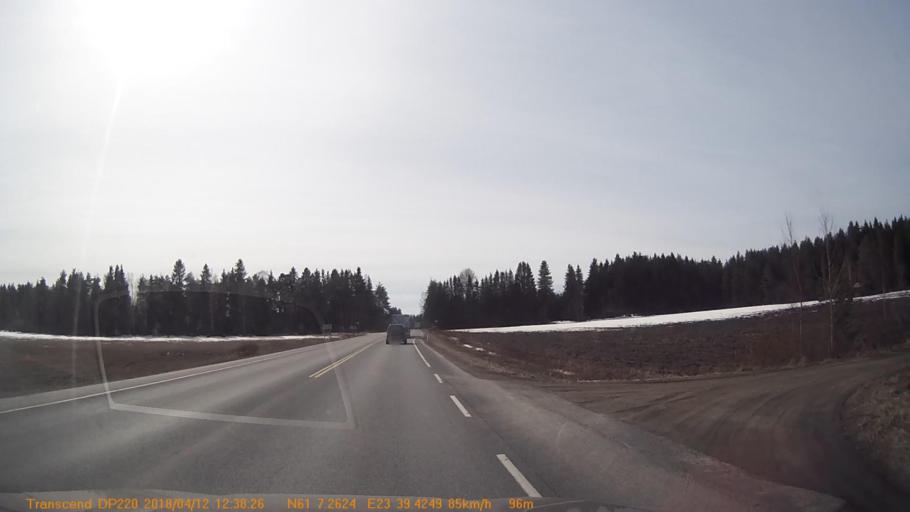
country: FI
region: Pirkanmaa
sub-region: Etelae-Pirkanmaa
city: Kylmaekoski
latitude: 61.1212
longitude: 23.6573
